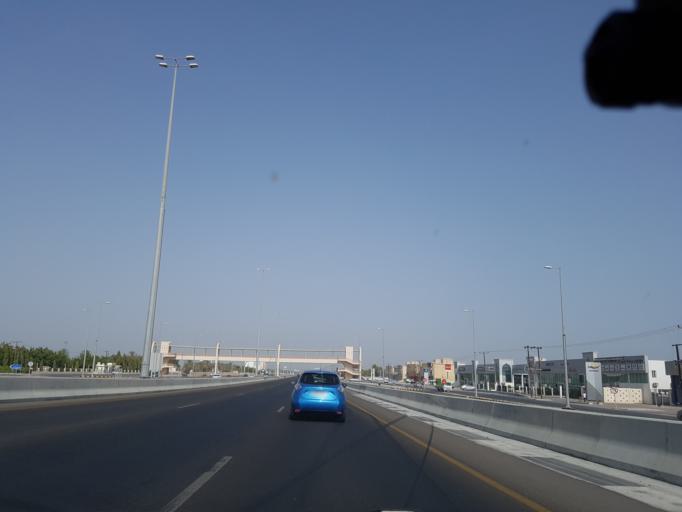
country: OM
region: Al Batinah
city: Barka'
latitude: 23.6685
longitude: 57.8786
